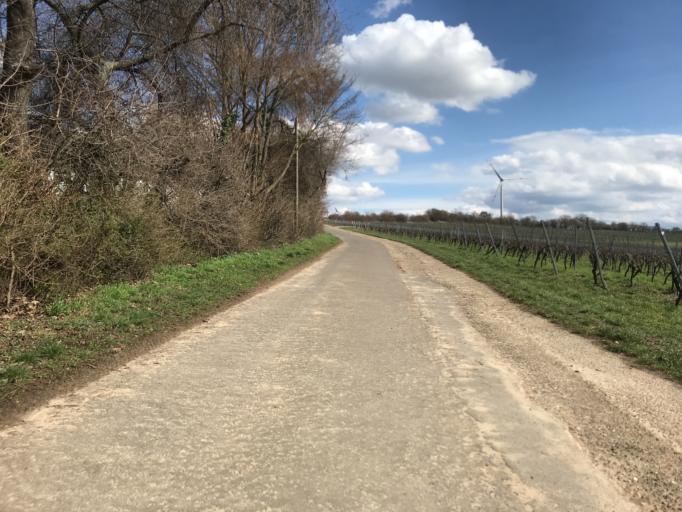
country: DE
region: Rheinland-Pfalz
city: Klein-Winternheim
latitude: 49.9395
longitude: 8.2200
